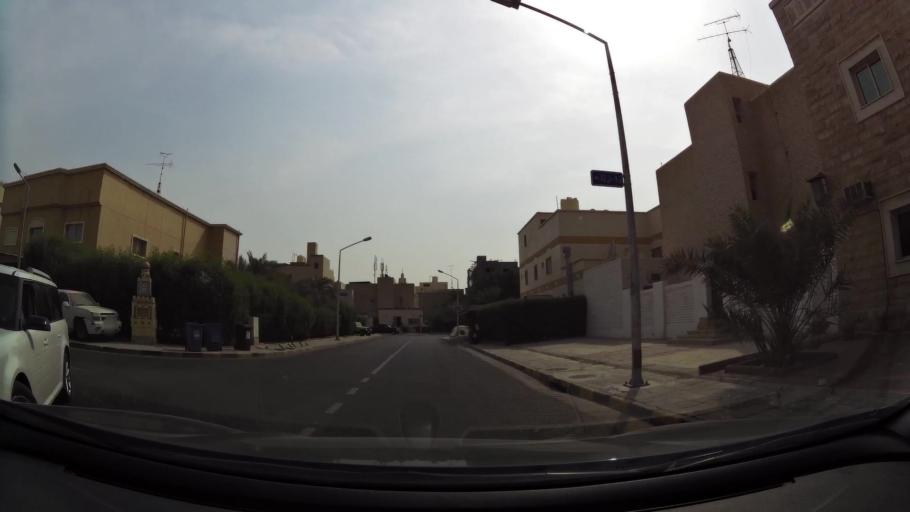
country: KW
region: Al Farwaniyah
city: Al Farwaniyah
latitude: 29.2843
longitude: 47.9464
